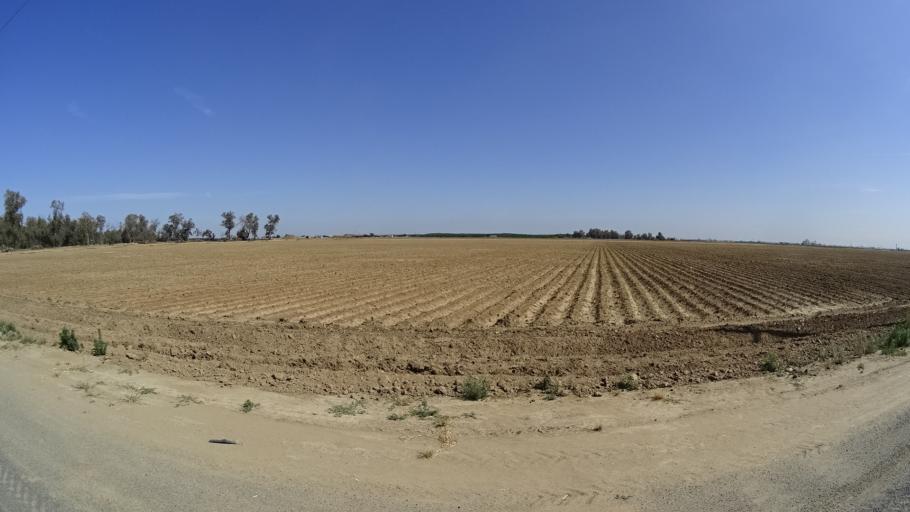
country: US
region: California
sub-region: Kings County
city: Home Garden
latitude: 36.2549
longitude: -119.6773
